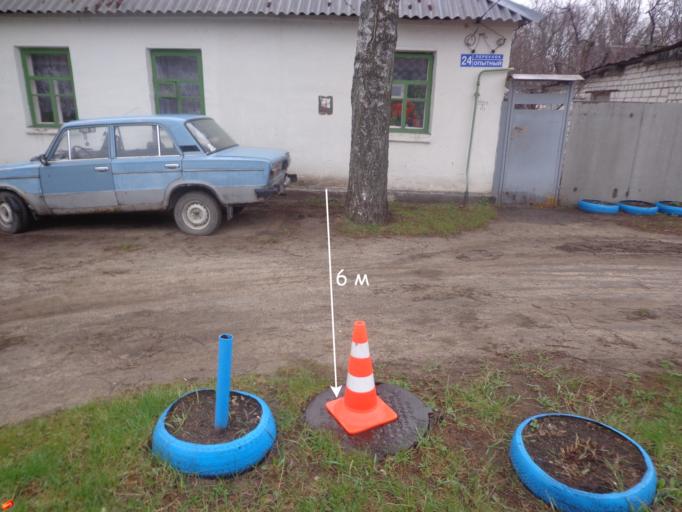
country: RU
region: Voronezj
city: Podgornoye
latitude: 51.7260
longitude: 39.1929
